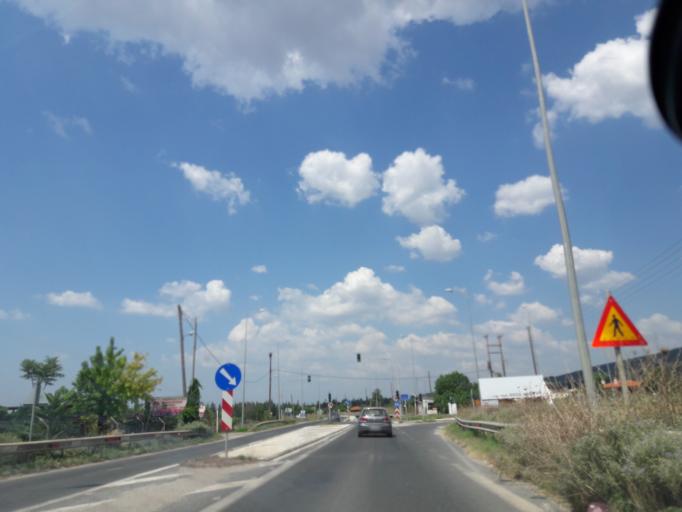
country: GR
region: Central Macedonia
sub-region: Nomos Thessalonikis
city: Souroti
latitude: 40.5058
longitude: 23.0901
